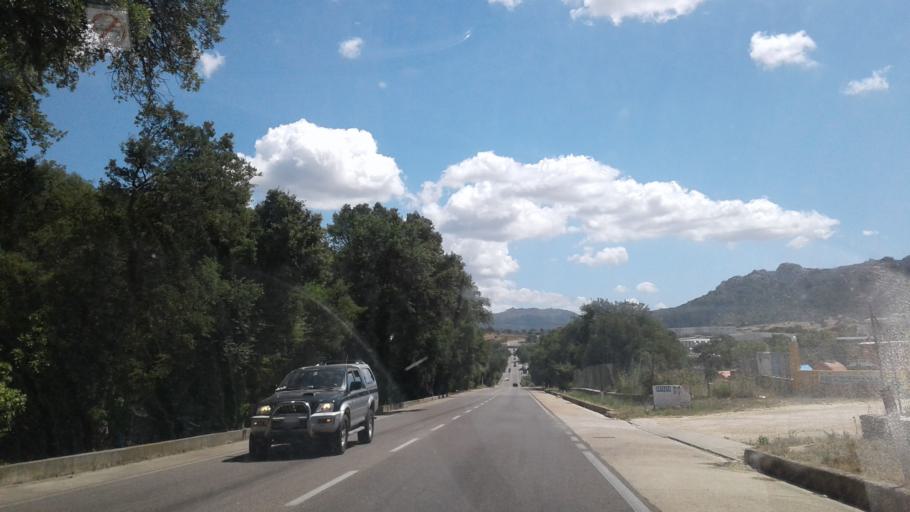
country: IT
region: Sardinia
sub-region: Provincia di Olbia-Tempio
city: Tempio Pausania
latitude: 40.9063
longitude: 9.1370
